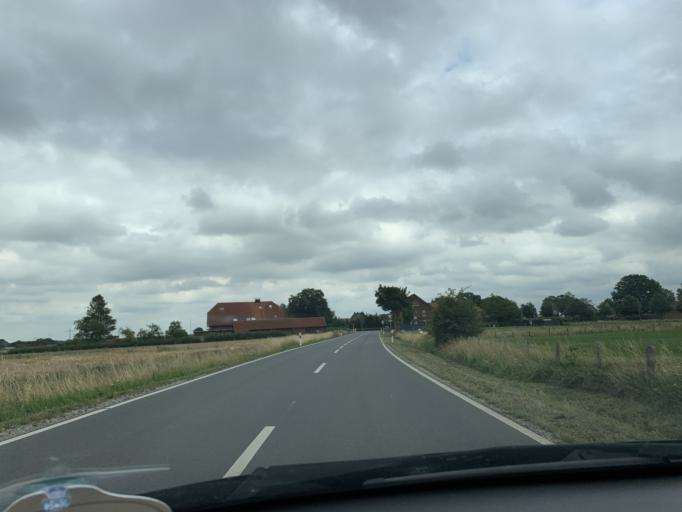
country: DE
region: North Rhine-Westphalia
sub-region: Regierungsbezirk Munster
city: Wadersloh
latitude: 51.7562
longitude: 8.2252
